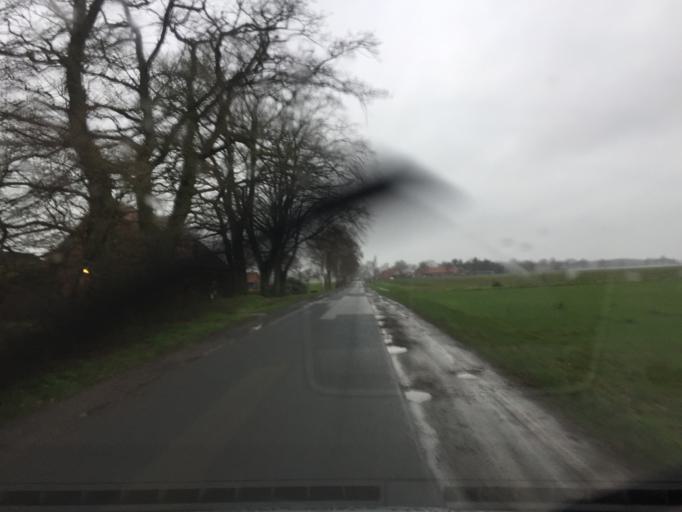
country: DE
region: Lower Saxony
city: Borstel
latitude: 52.6050
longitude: 8.9470
